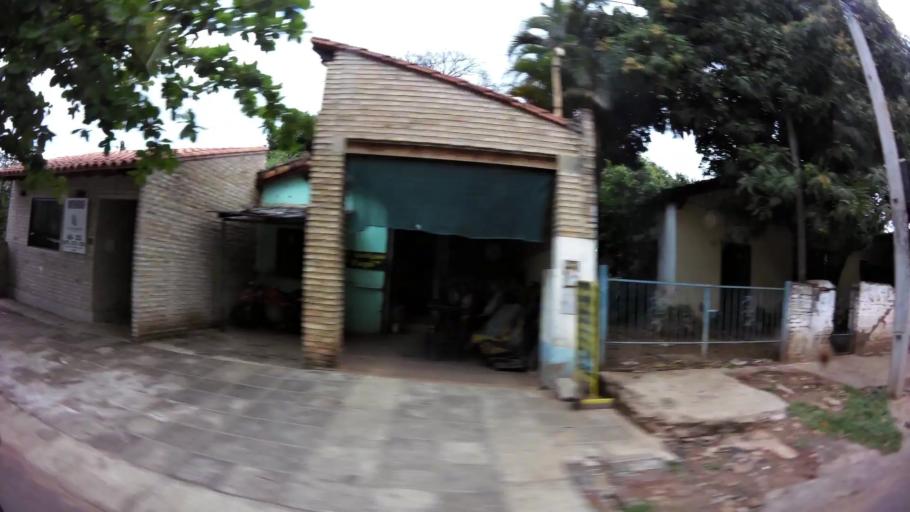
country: PY
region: Central
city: San Lorenzo
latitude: -25.2675
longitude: -57.5016
